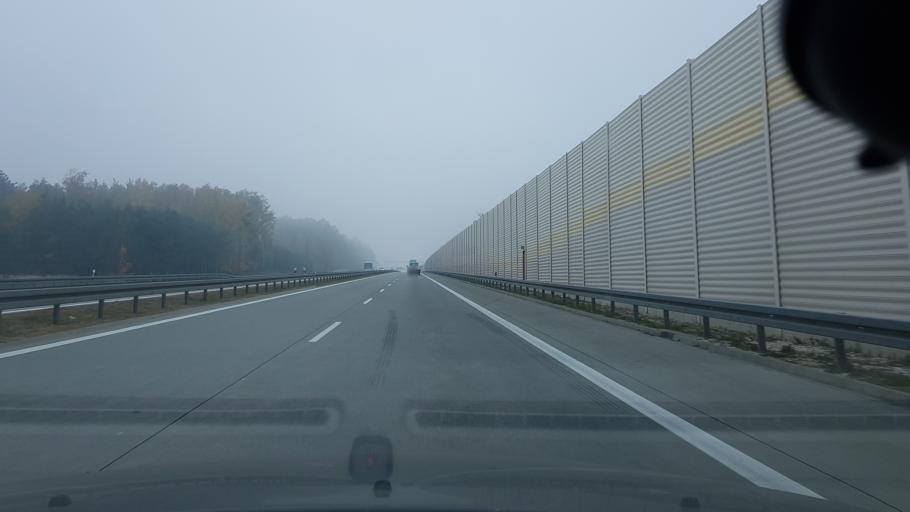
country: PL
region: Lodz Voivodeship
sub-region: Powiat rawski
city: Rawa Mazowiecka
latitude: 51.8138
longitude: 20.3114
